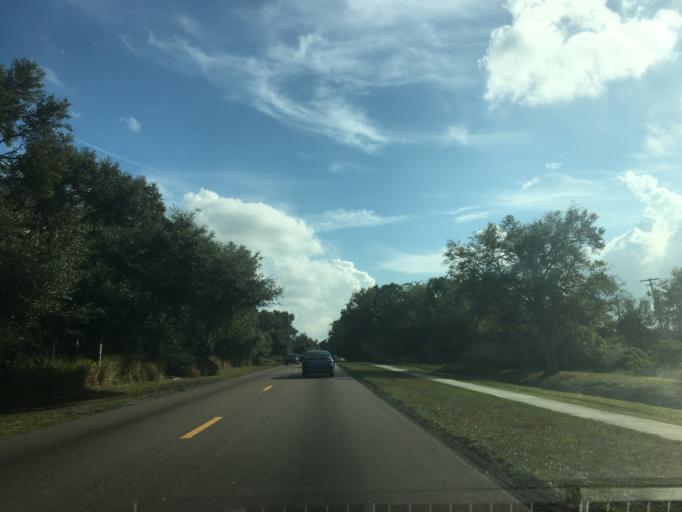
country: US
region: Florida
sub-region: Hillsborough County
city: Temple Terrace
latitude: 28.0142
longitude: -82.4312
